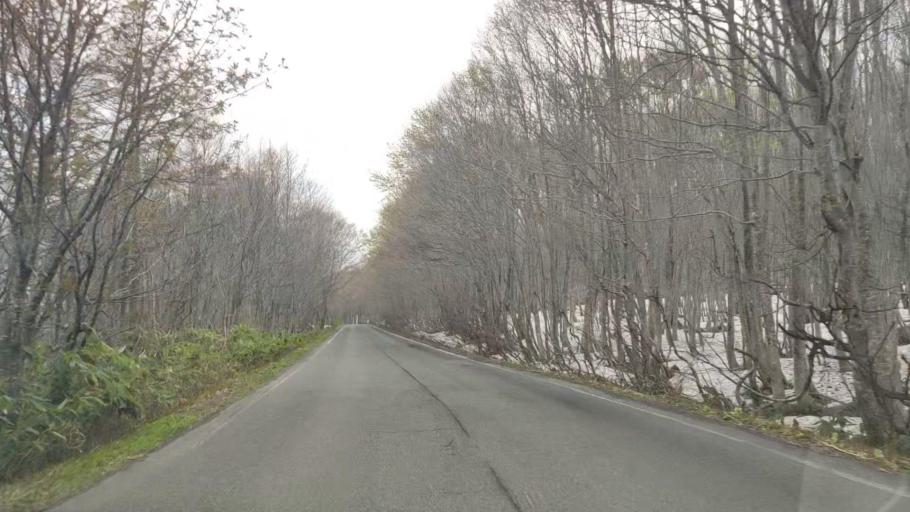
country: JP
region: Aomori
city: Aomori Shi
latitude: 40.6841
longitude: 140.9265
